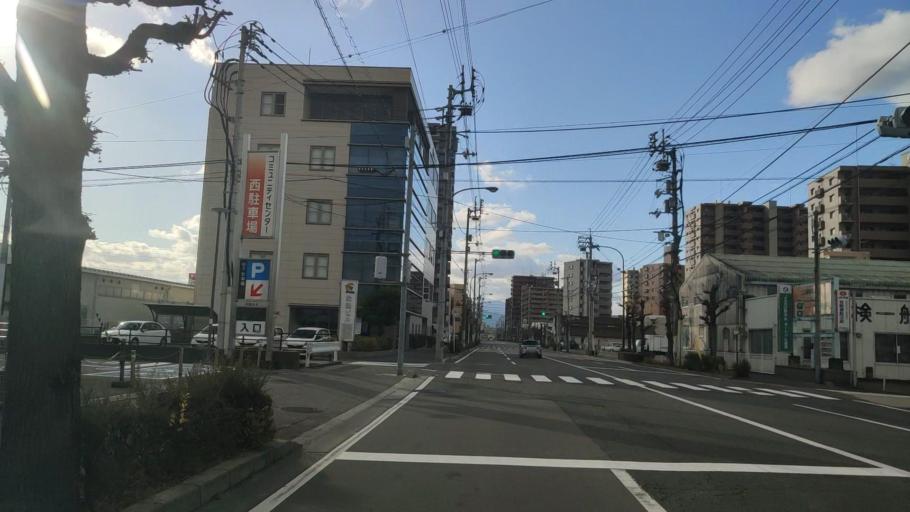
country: JP
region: Ehime
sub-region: Shikoku-chuo Shi
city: Matsuyama
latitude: 33.8357
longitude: 132.7525
